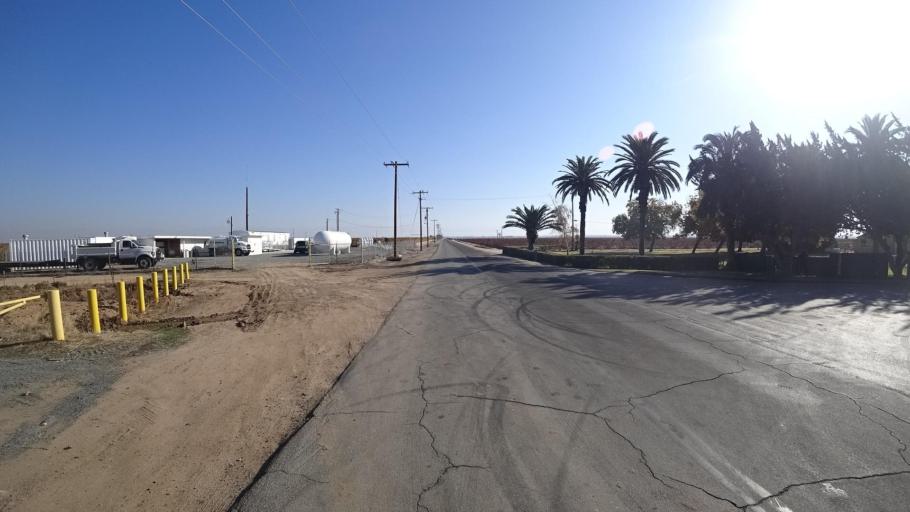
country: US
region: California
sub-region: Kern County
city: Delano
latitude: 35.7470
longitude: -119.1743
